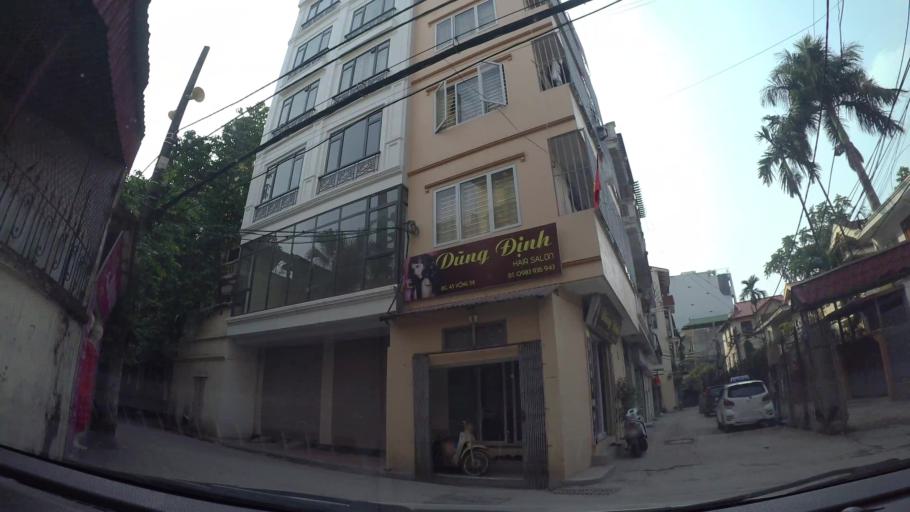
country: VN
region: Ha Noi
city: Tay Ho
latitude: 21.0517
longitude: 105.8115
